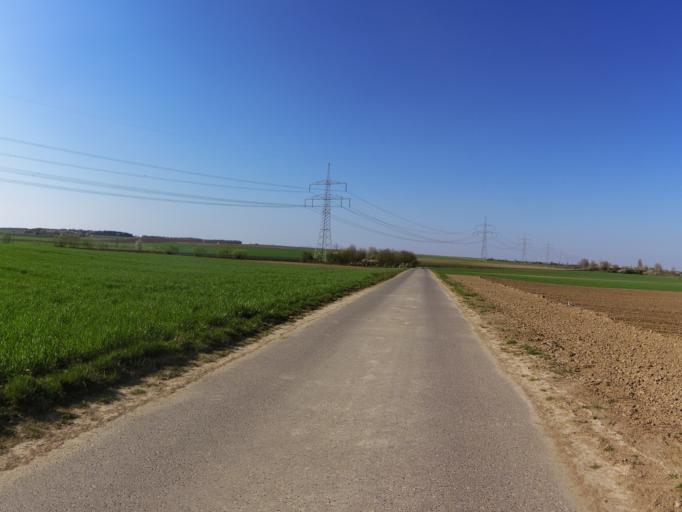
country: DE
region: Bavaria
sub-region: Regierungsbezirk Unterfranken
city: Oberpleichfeld
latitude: 49.8290
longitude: 10.0909
